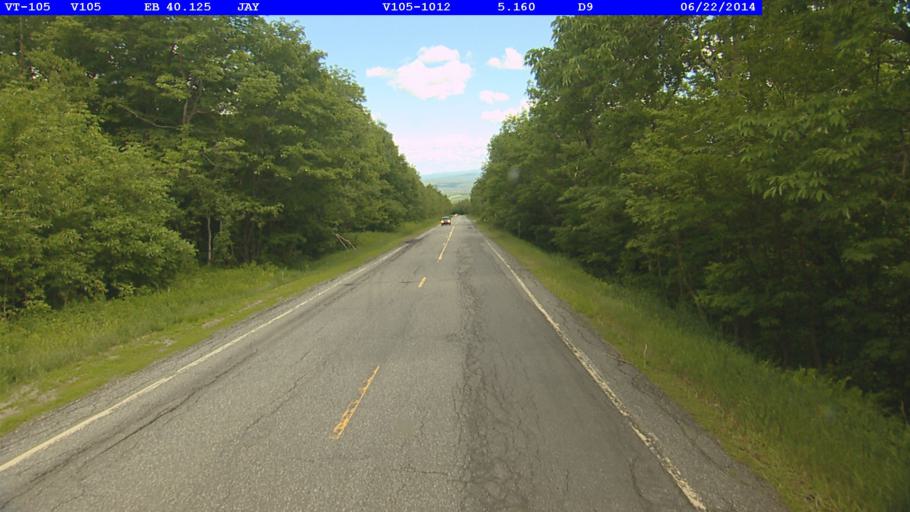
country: CA
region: Quebec
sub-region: Monteregie
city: Sutton
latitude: 44.9793
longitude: -72.4822
